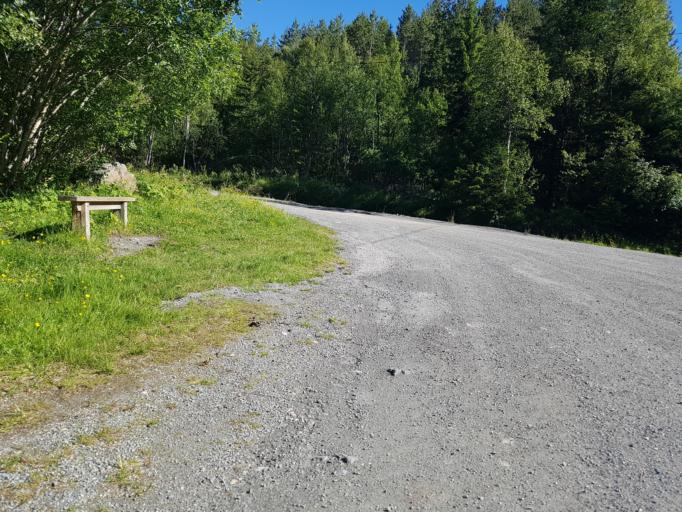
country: NO
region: Sor-Trondelag
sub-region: Trondheim
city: Trondheim
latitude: 63.4337
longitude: 10.2729
